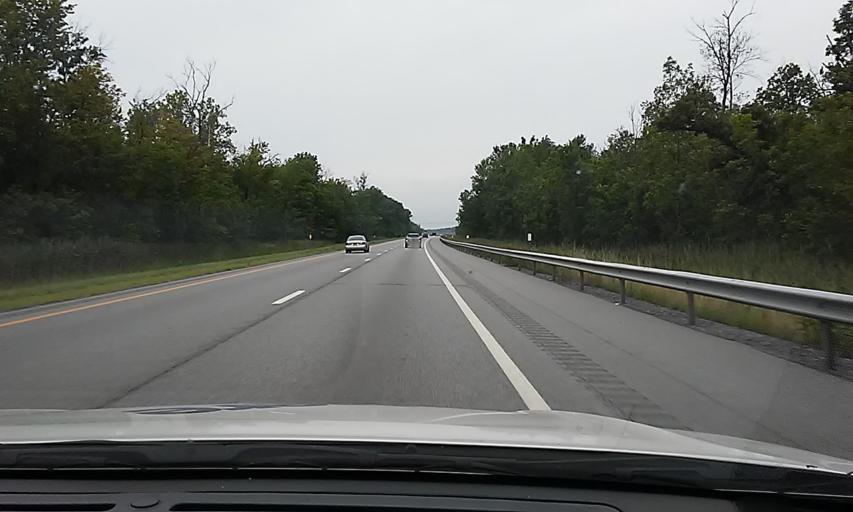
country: US
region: New York
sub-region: Erie County
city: Clarence
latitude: 42.9677
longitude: -78.5338
